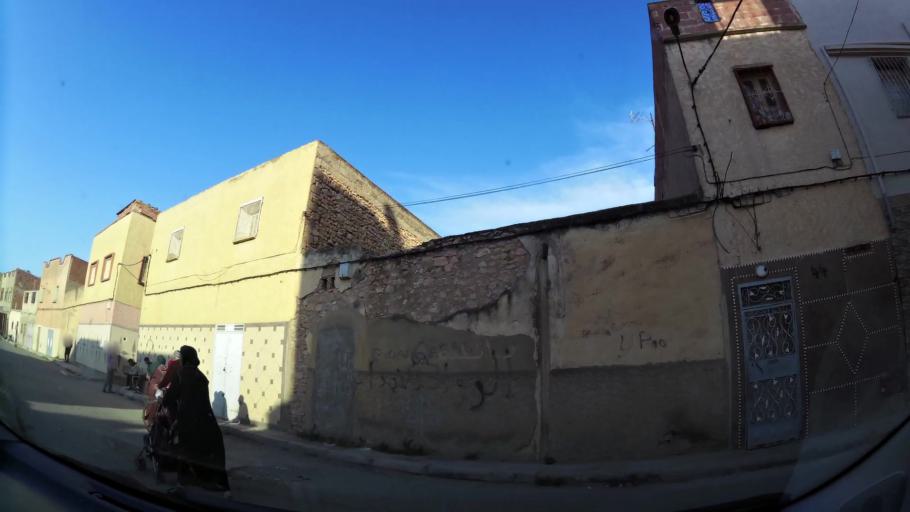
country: MA
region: Oriental
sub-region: Oujda-Angad
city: Oujda
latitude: 34.7035
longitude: -1.9087
